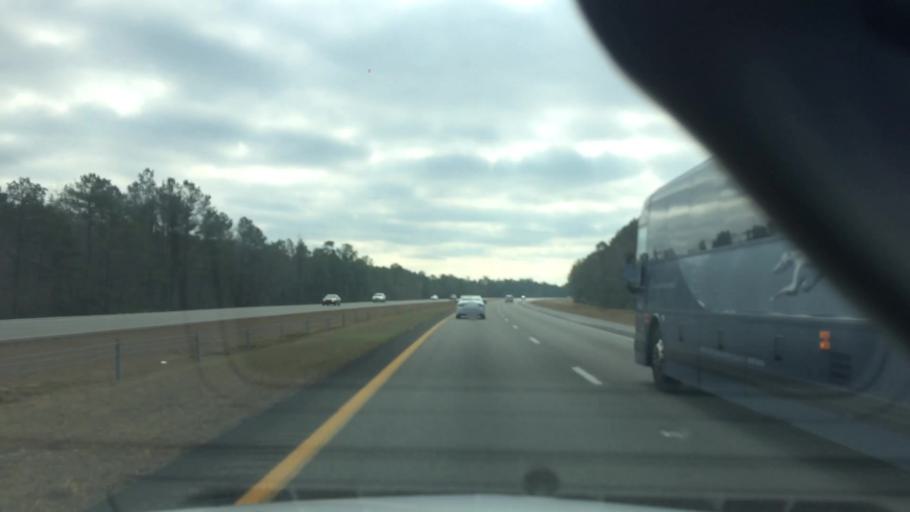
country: US
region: North Carolina
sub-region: New Hanover County
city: Castle Hayne
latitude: 34.3925
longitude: -77.8749
